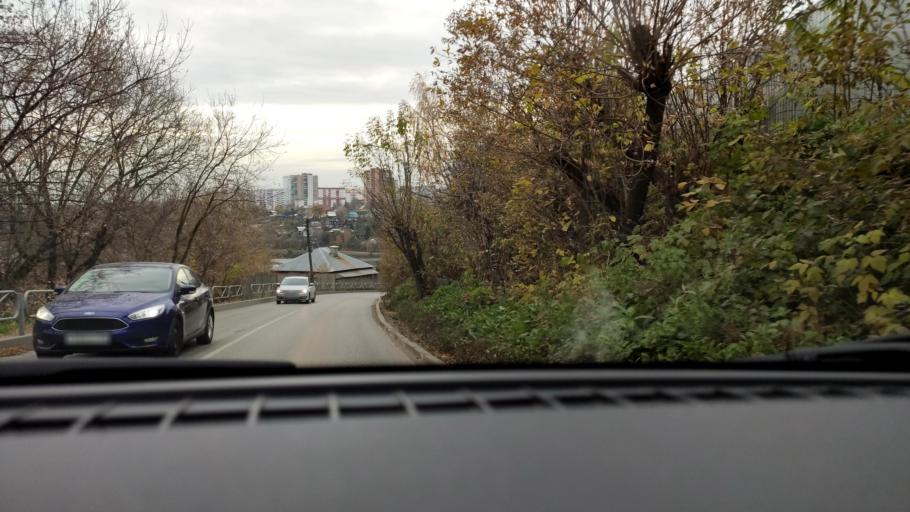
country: RU
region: Perm
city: Perm
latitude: 58.0424
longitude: 56.3270
